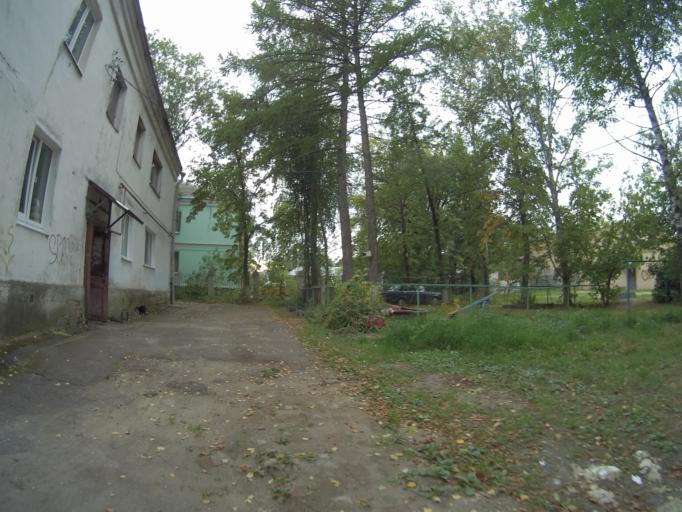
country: RU
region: Vladimir
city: Vladimir
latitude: 56.1243
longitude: 40.3607
